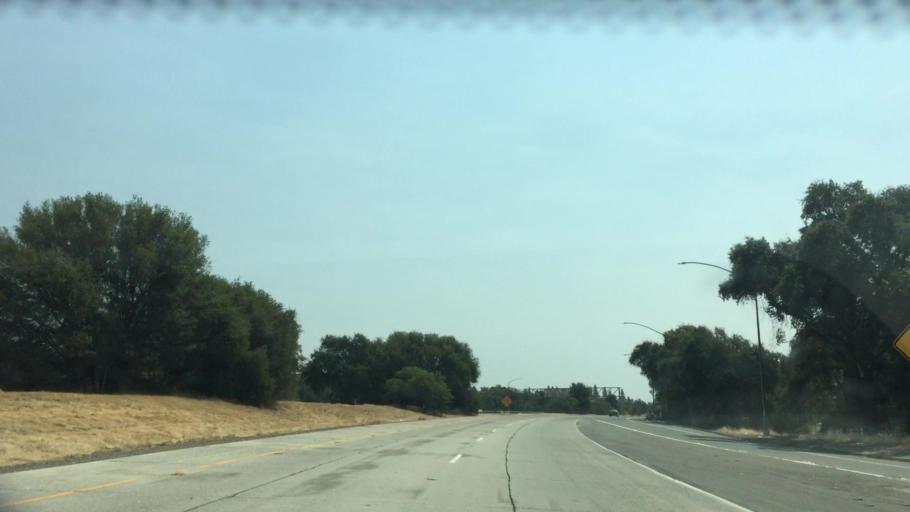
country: US
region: California
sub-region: Sacramento County
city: Foothill Farms
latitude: 38.6467
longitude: -121.3718
